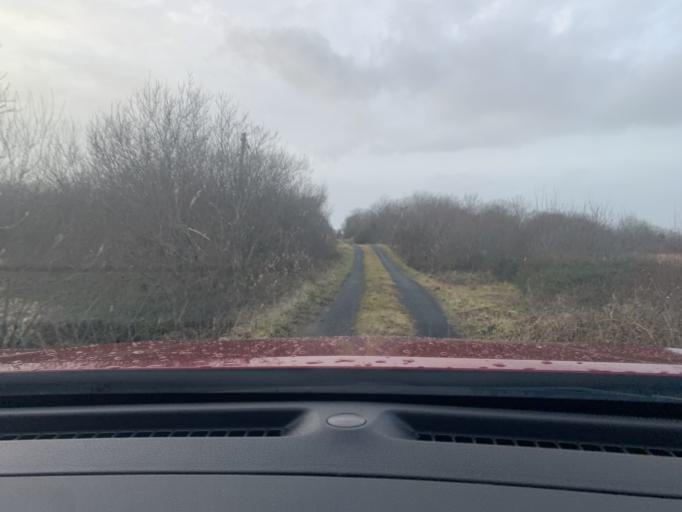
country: IE
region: Connaught
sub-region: Roscommon
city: Ballaghaderreen
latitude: 53.9520
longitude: -8.5348
